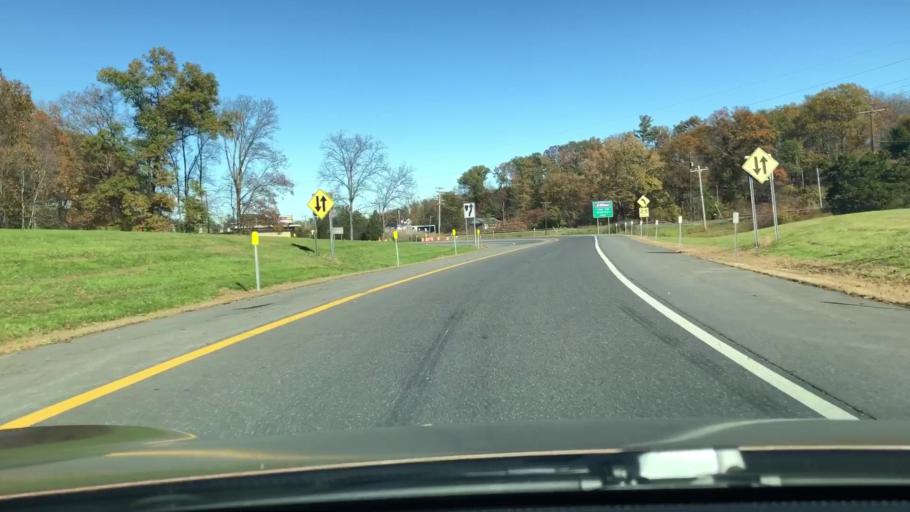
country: US
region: New York
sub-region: Ulster County
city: Saugerties
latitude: 42.0808
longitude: -73.9727
